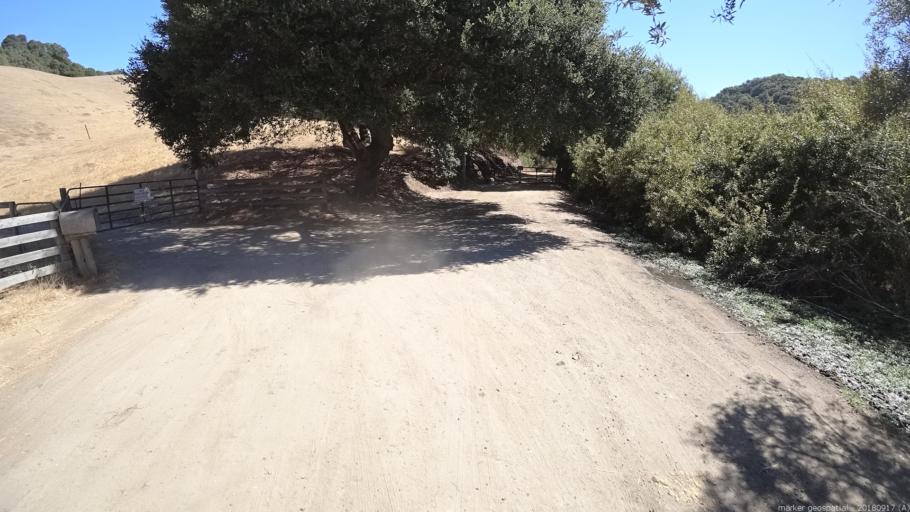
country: US
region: California
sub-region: San Benito County
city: San Juan Bautista
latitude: 36.8058
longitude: -121.5617
